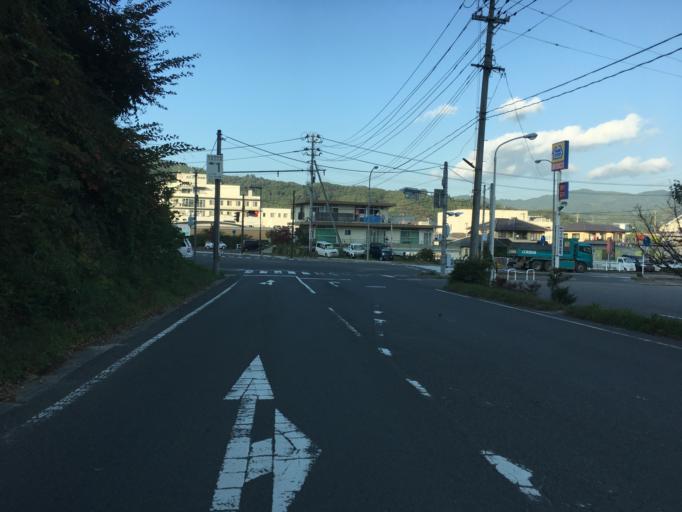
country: JP
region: Fukushima
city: Fukushima-shi
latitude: 37.6622
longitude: 140.5953
